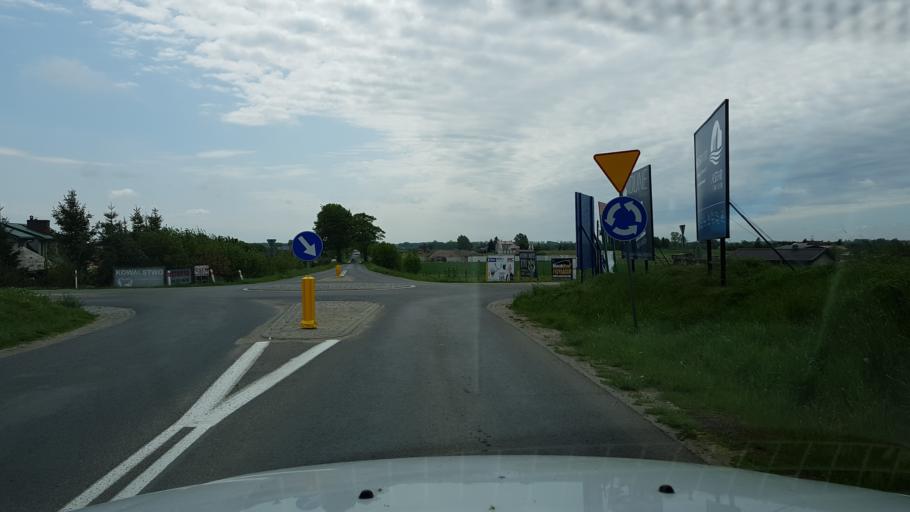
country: PL
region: West Pomeranian Voivodeship
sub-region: Powiat koszalinski
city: Mielno
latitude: 54.2388
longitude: 15.9730
